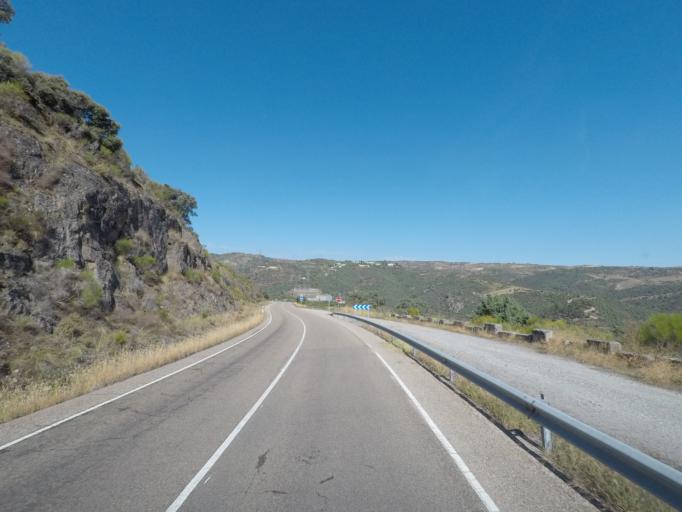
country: ES
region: Castille and Leon
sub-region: Provincia de Salamanca
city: Villarino de los Aires
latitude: 41.2959
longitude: -6.4631
